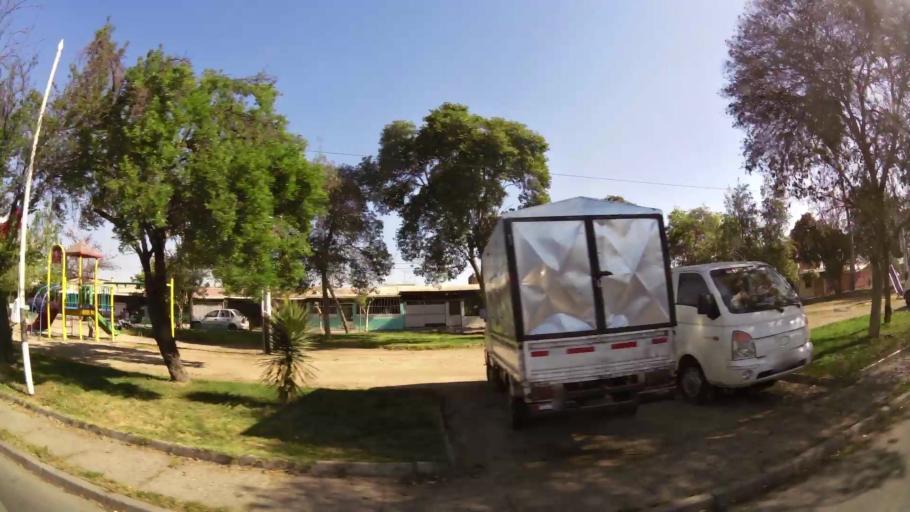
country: CL
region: Santiago Metropolitan
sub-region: Provincia de Santiago
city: Santiago
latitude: -33.5032
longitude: -70.6921
